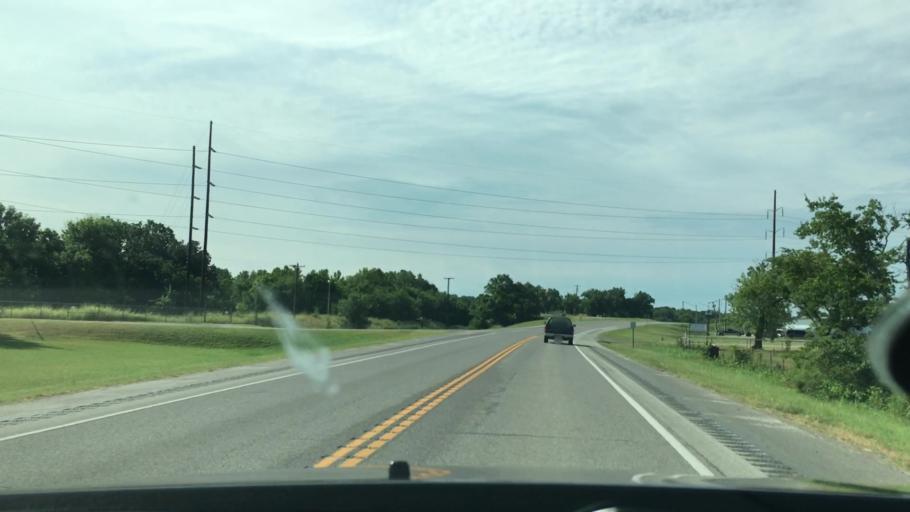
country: US
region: Oklahoma
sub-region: Murray County
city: Sulphur
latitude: 34.5236
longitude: -96.9695
